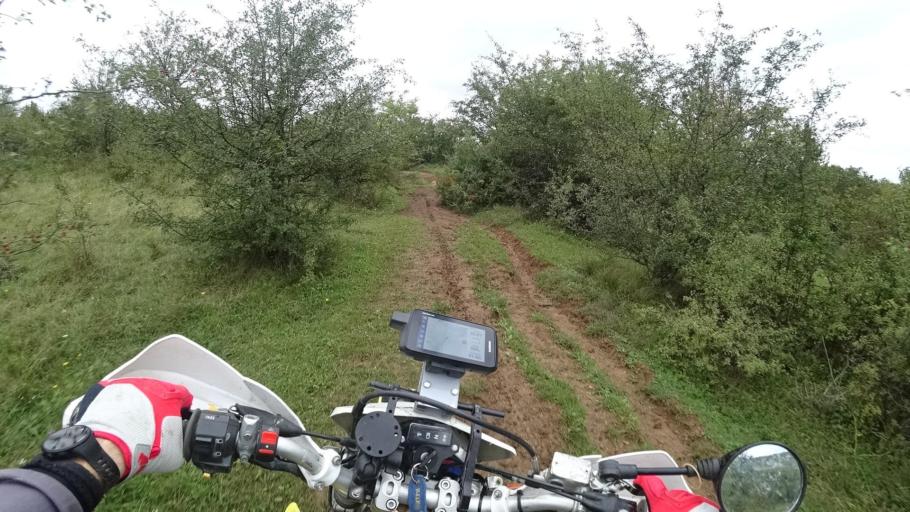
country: BA
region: Republika Srpska
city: Bronzani Majdan
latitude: 44.6852
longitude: 16.9692
